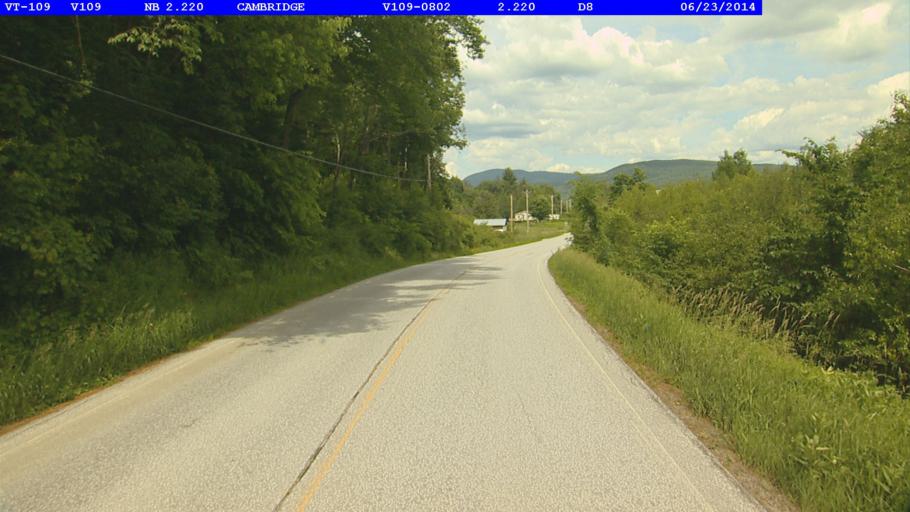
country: US
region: Vermont
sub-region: Lamoille County
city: Johnson
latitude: 44.6701
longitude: -72.7967
